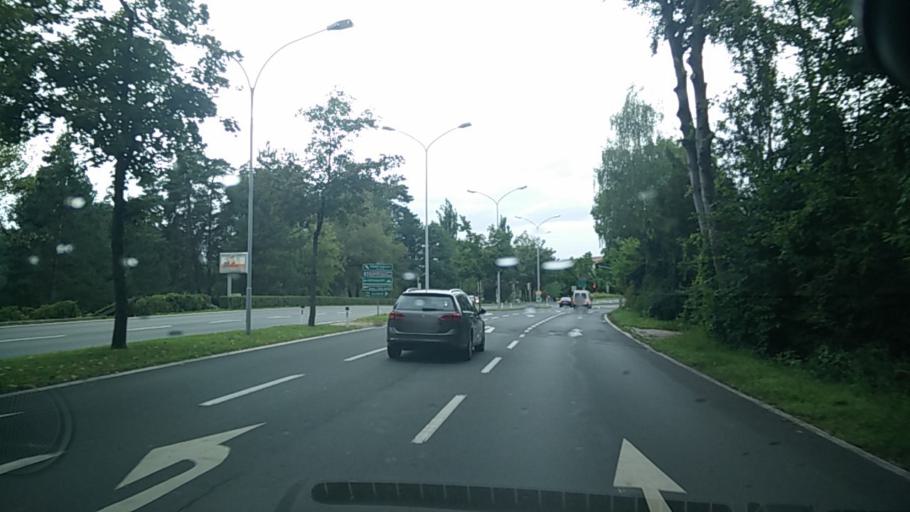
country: AT
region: Carinthia
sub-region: Klagenfurt am Woerthersee
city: Klagenfurt am Woerthersee
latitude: 46.6218
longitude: 14.2607
